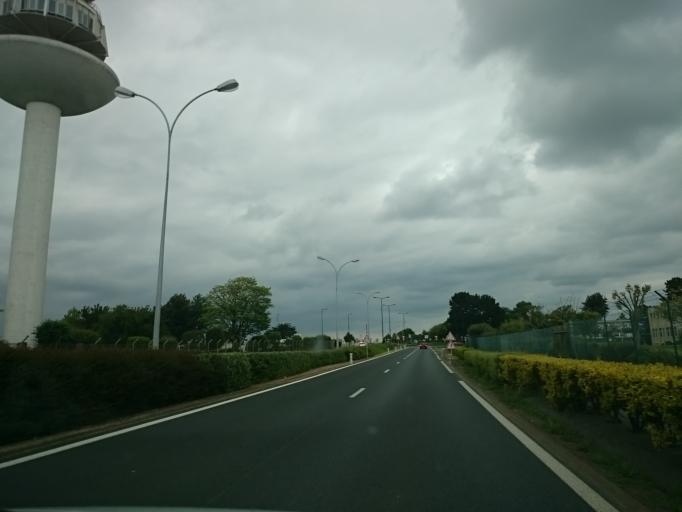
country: FR
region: Brittany
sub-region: Departement des Cotes-d'Armor
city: Lannion
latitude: 48.7567
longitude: -3.4550
